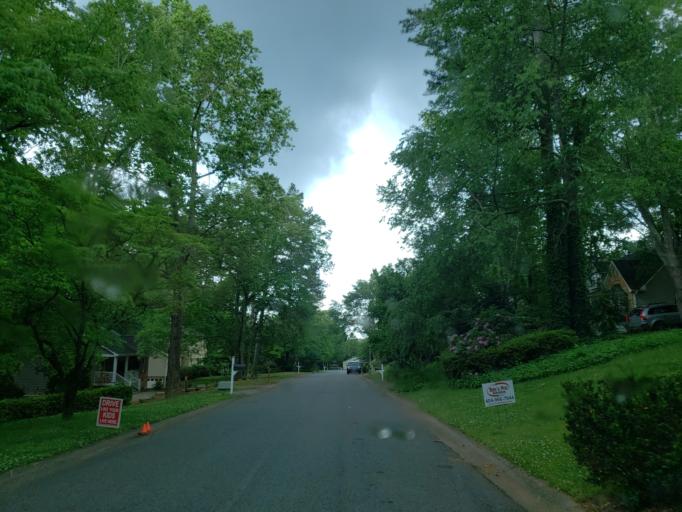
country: US
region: Georgia
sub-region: Cobb County
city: Marietta
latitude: 33.9574
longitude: -84.5707
